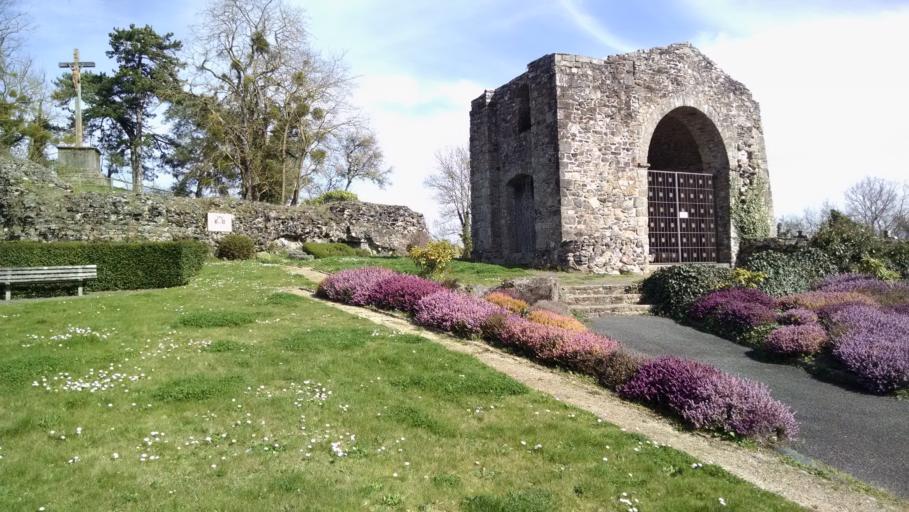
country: FR
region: Pays de la Loire
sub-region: Departement de la Loire-Atlantique
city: Le Pallet
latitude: 47.1360
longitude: -1.3310
